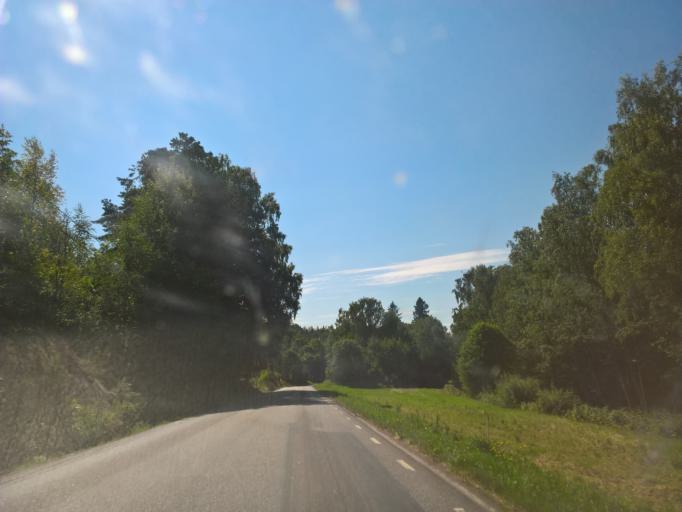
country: SE
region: OEstergoetland
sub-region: Finspangs Kommun
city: Finspang
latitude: 58.7242
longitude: 15.8320
